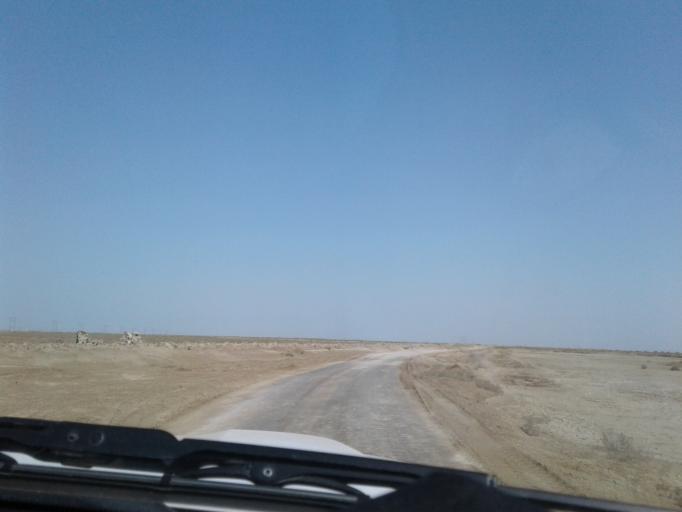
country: IR
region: Golestan
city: Gomishan
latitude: 37.8228
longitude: 53.9216
